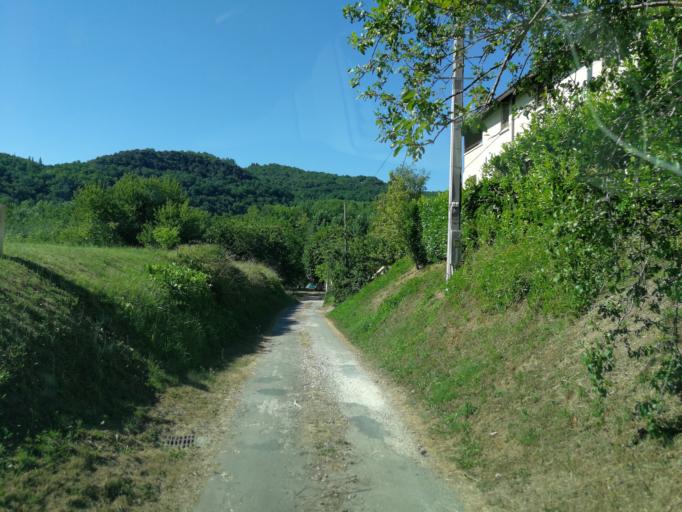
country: FR
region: Aquitaine
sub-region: Departement de la Dordogne
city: Eyvigues-et-Eybenes
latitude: 44.8651
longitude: 1.3674
